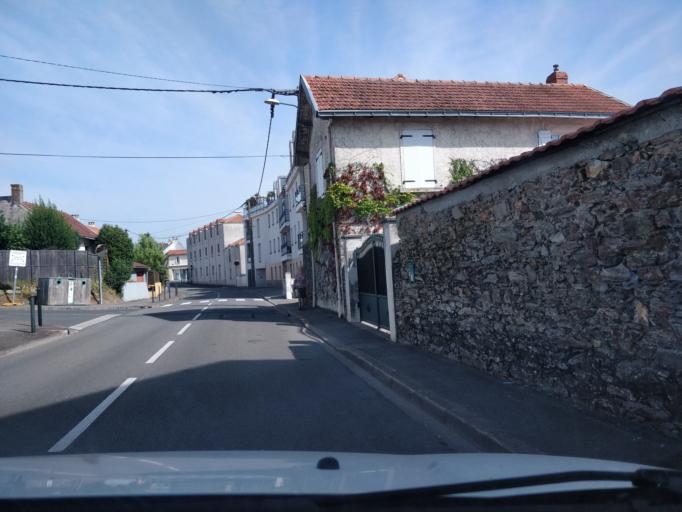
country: FR
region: Pays de la Loire
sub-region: Departement de la Loire-Atlantique
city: Saint-Sebastien-sur-Loire
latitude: 47.2068
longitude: -1.4993
